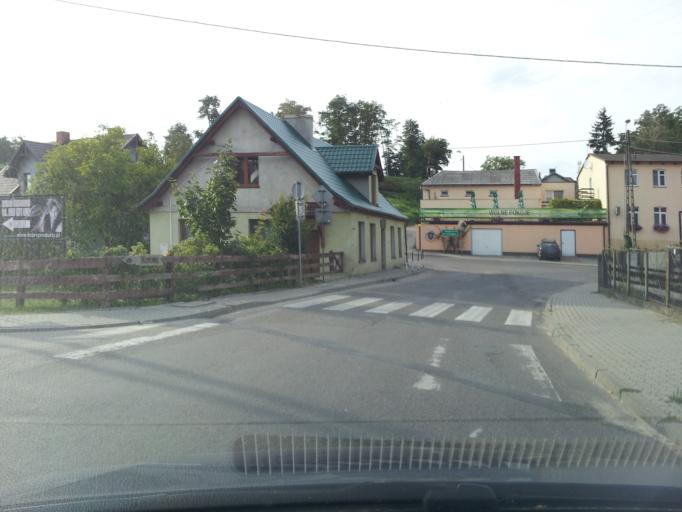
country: PL
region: Kujawsko-Pomorskie
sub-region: Powiat brodnicki
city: Gorzno
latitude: 53.1985
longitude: 19.6416
